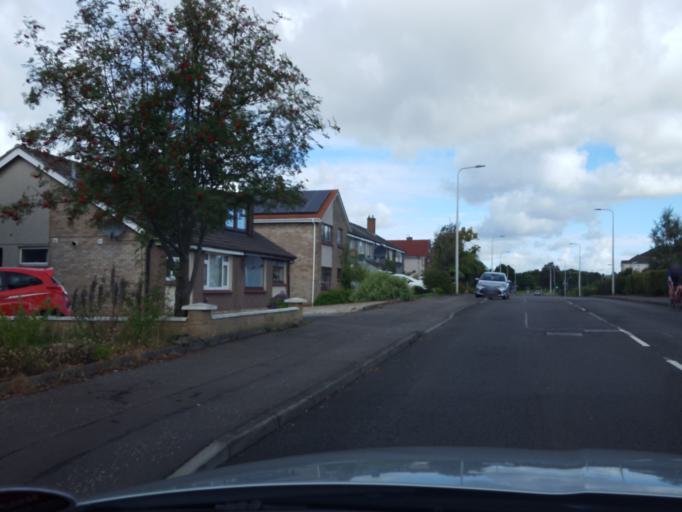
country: GB
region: Scotland
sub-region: Fife
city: Rosyth
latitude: 56.0572
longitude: -3.4155
